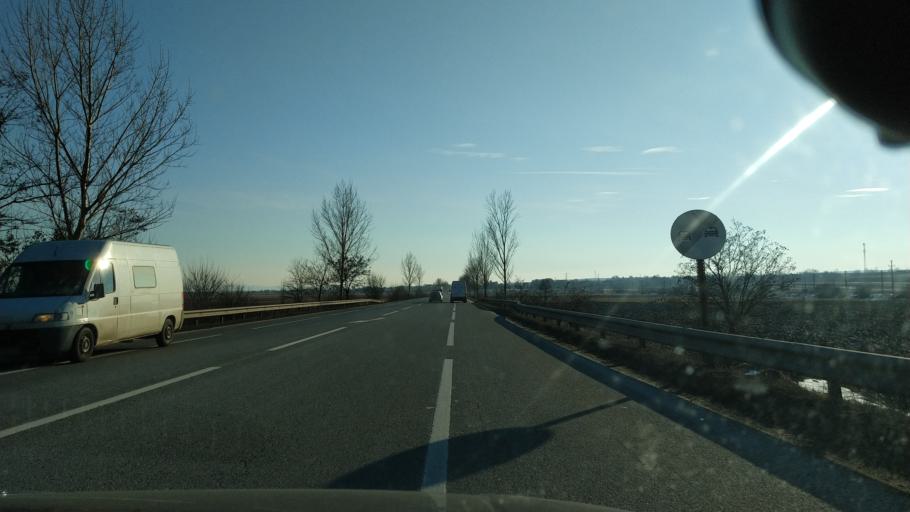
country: RO
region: Bacau
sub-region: Comuna Filipesti
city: Filipesti
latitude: 46.7633
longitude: 26.8816
